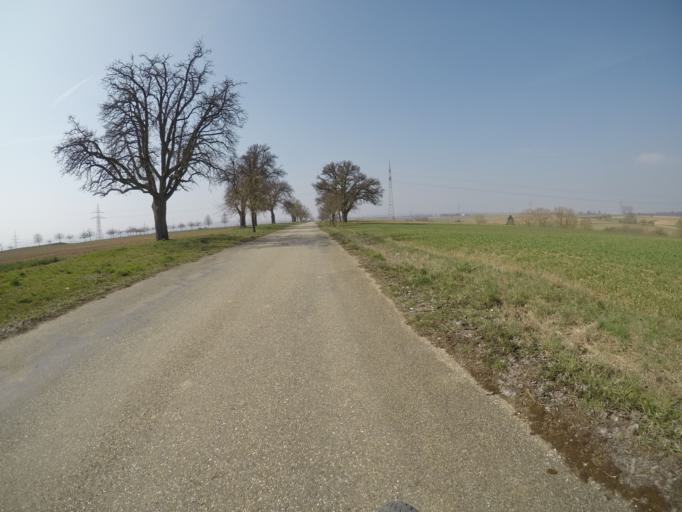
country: DE
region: Baden-Wuerttemberg
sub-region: Regierungsbezirk Stuttgart
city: Nufringen
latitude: 48.6182
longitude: 8.8753
